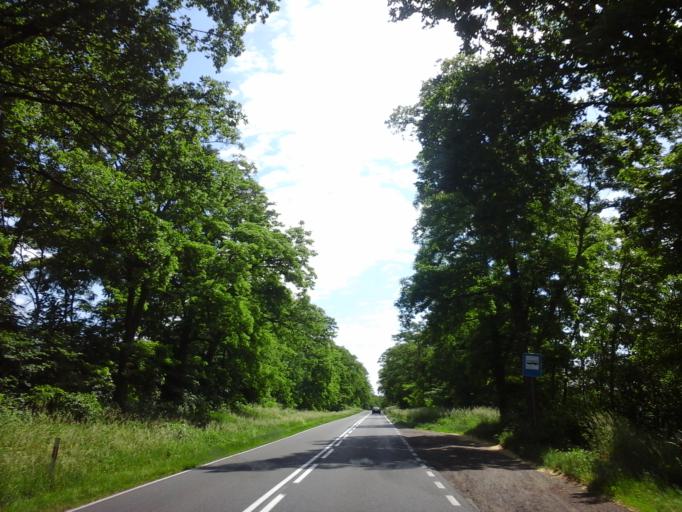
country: PL
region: West Pomeranian Voivodeship
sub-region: Powiat stargardzki
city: Suchan
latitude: 53.2027
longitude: 15.3341
